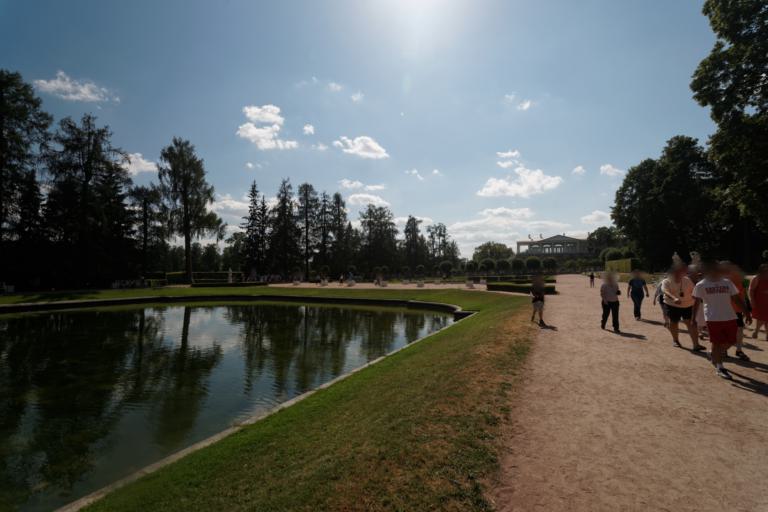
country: RU
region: St.-Petersburg
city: Pushkin
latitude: 59.7160
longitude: 30.3979
